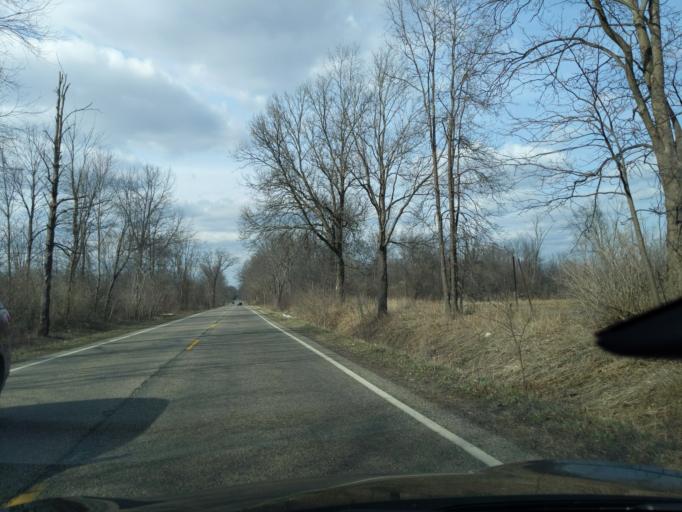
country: US
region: Michigan
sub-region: Jackson County
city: Jackson
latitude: 42.3170
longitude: -84.4136
